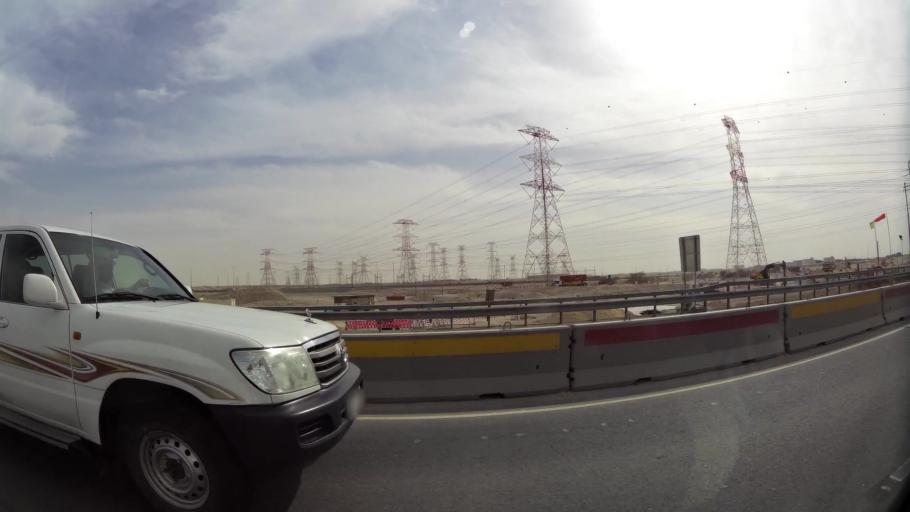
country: QA
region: Baladiyat ar Rayyan
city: Ash Shahaniyah
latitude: 25.3416
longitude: 51.3154
